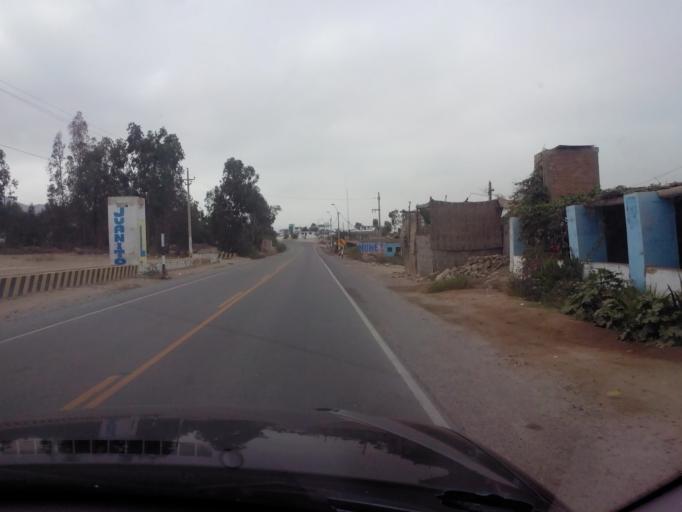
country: PE
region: Ica
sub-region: Provincia de Pisco
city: Humay
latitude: -13.7264
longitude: -75.9445
